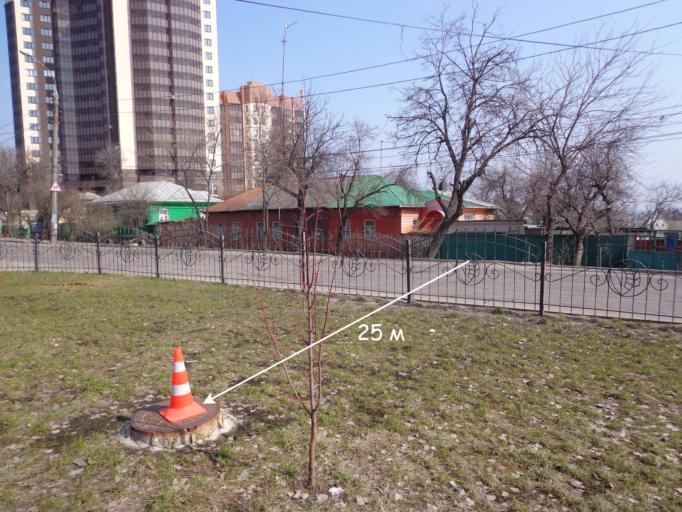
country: RU
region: Voronezj
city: Voronezh
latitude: 51.7077
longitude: 39.2302
